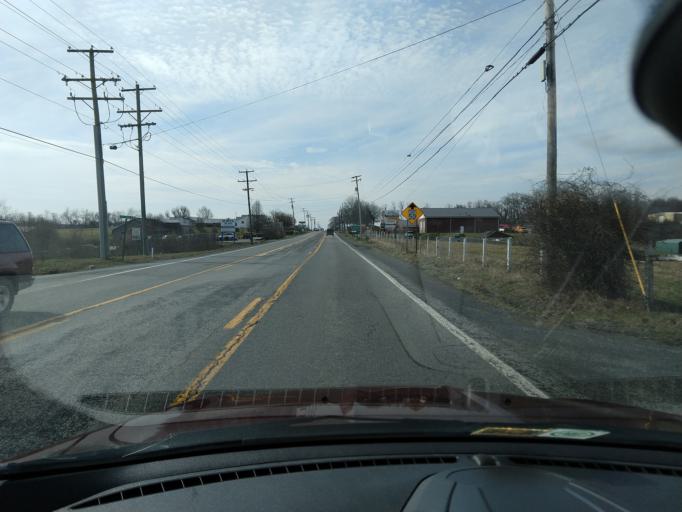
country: US
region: West Virginia
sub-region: Greenbrier County
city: Lewisburg
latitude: 37.8352
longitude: -80.4170
